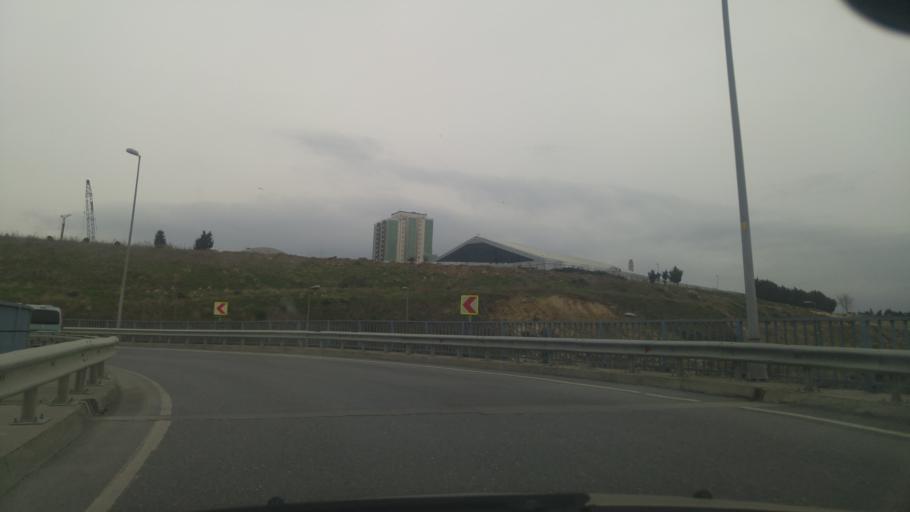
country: TR
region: Istanbul
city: Mahmutbey
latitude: 41.0121
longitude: 28.7715
